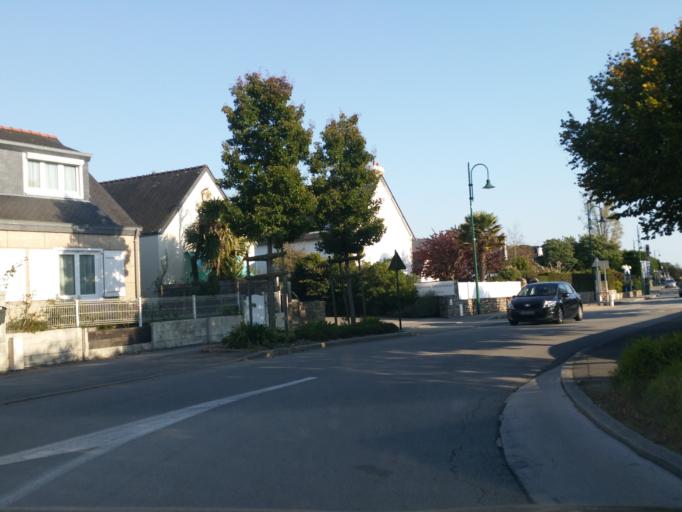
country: FR
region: Brittany
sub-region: Departement du Morbihan
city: Carnac
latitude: 47.5870
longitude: -3.0772
